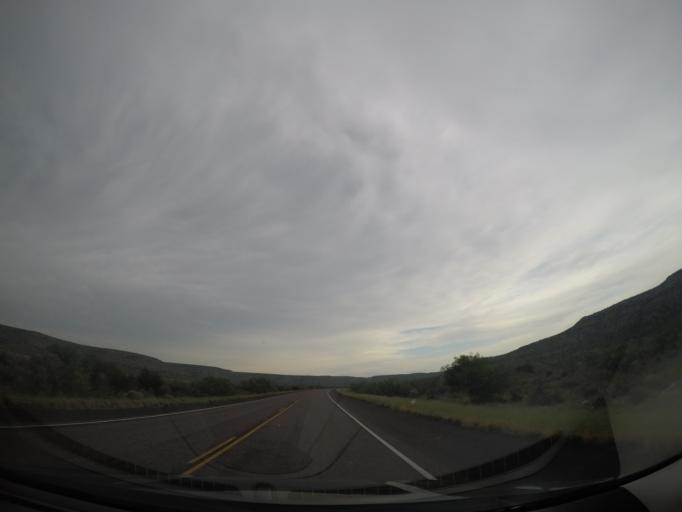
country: US
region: Texas
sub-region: Terrell County
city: Sanderson
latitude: 30.1683
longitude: -102.4731
